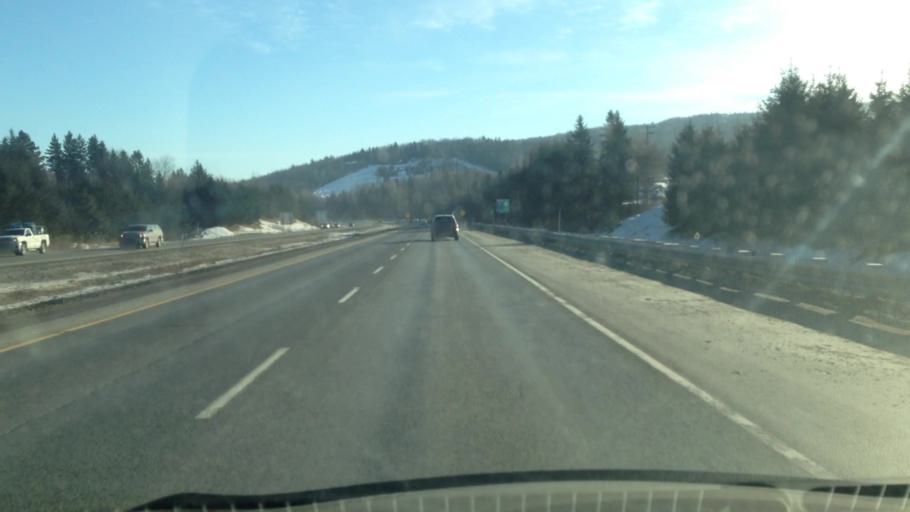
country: CA
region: Quebec
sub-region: Laurentides
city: Saint-Sauveur
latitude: 45.8874
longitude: -74.1351
